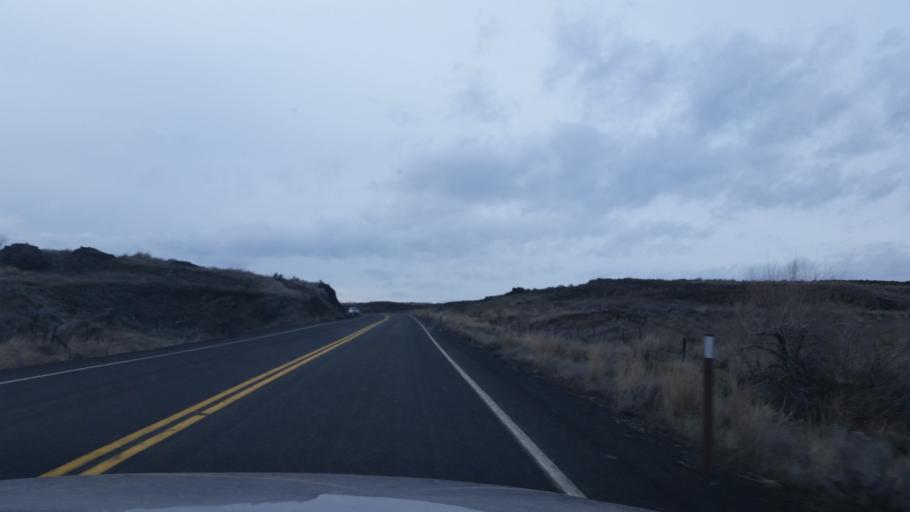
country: US
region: Washington
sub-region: Spokane County
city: Medical Lake
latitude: 47.2720
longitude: -117.9490
